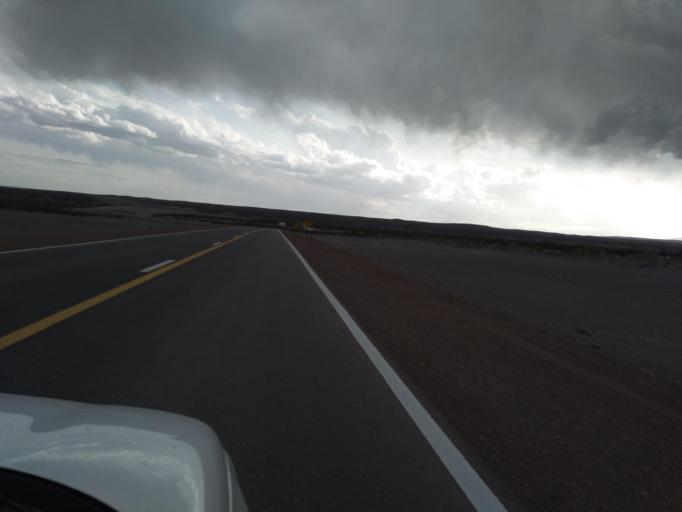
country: AR
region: Mendoza
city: La Consulta
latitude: -34.5441
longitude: -69.1636
